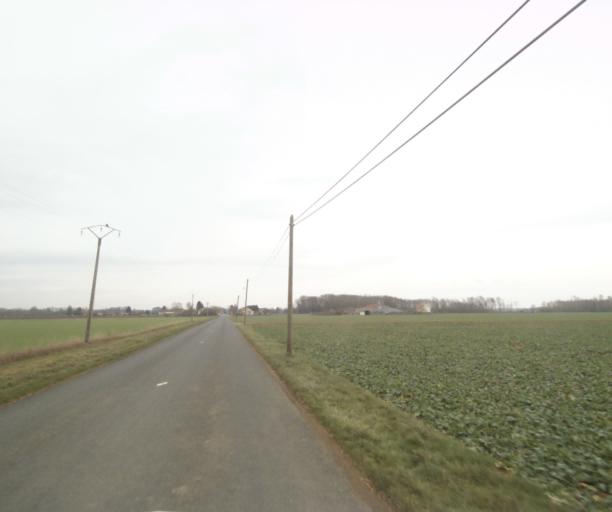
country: FR
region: Champagne-Ardenne
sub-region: Departement de la Haute-Marne
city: Villiers-en-Lieu
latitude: 48.6371
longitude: 4.8650
